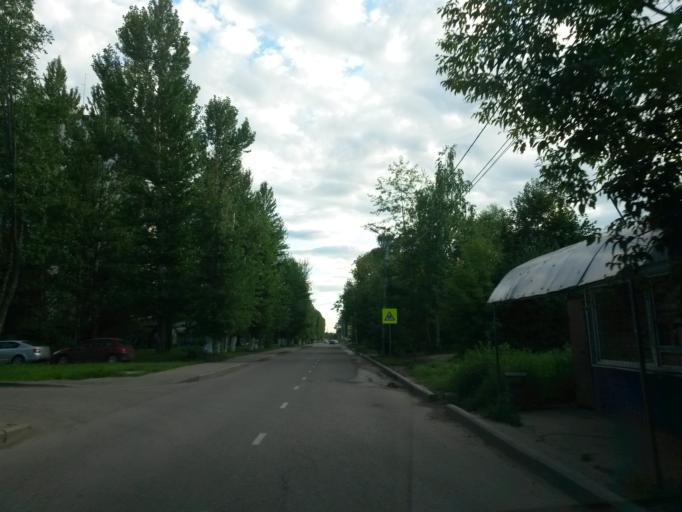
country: RU
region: Jaroslavl
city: Yaroslavl
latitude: 57.6881
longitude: 39.7763
